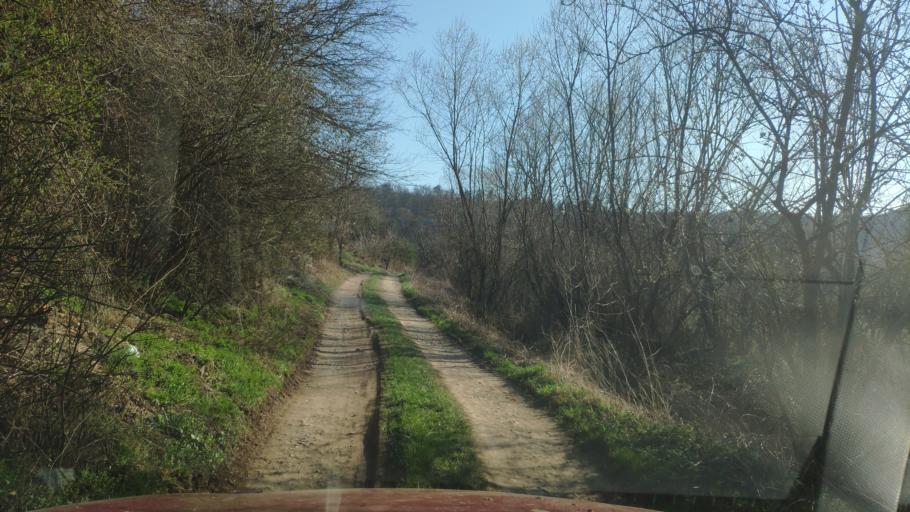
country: SK
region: Banskobystricky
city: Revuca
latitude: 48.5405
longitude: 20.2416
